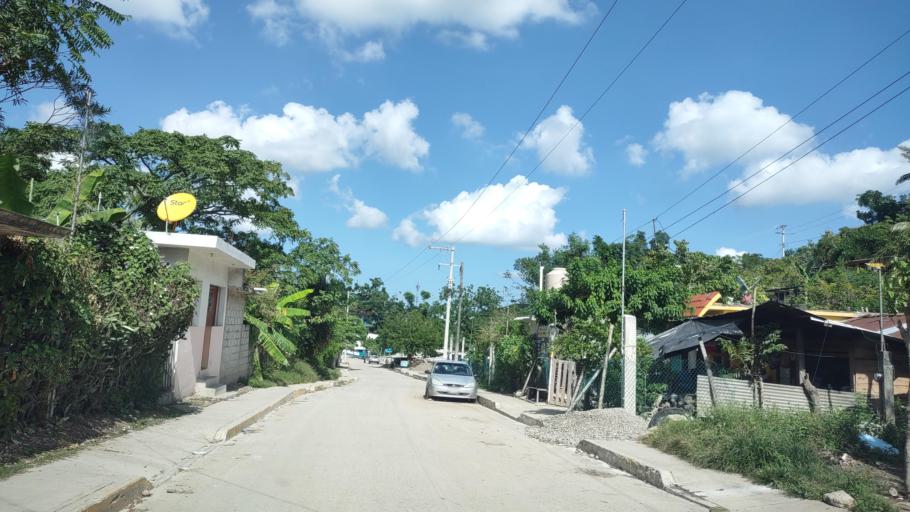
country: MM
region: Shan
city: Taunggyi
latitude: 20.5829
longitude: 97.3766
